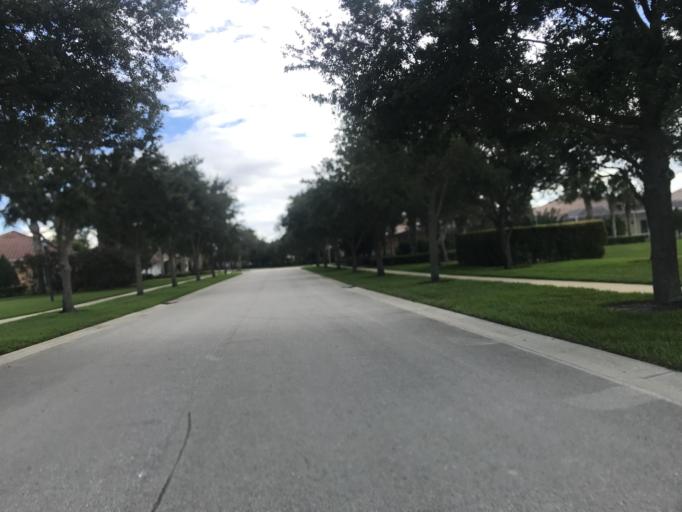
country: US
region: Florida
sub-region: Indian River County
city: Gifford
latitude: 27.6890
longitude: -80.4425
